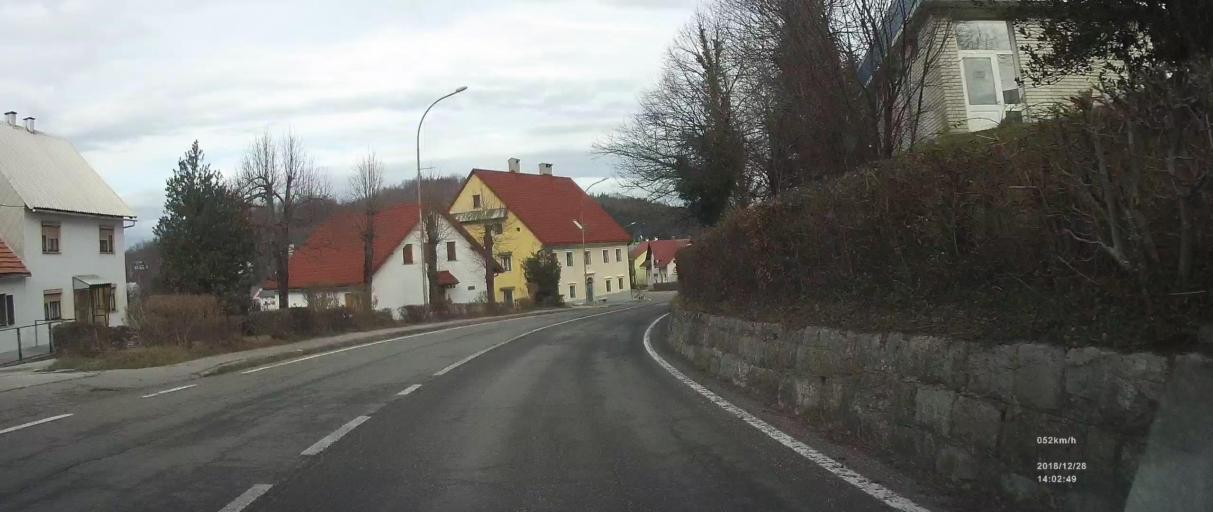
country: SI
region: Kostel
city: Kostel
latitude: 45.4319
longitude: 14.9047
